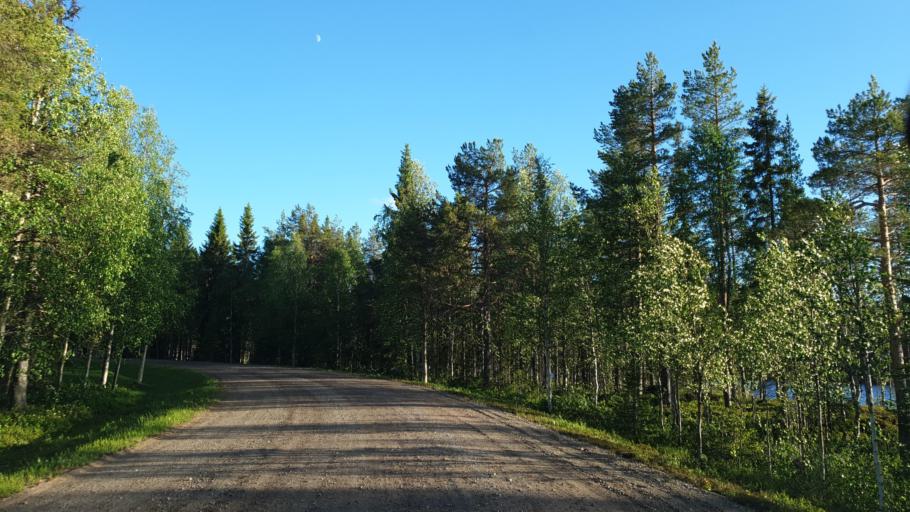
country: SE
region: Norrbotten
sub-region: Arvidsjaurs Kommun
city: Arvidsjaur
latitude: 65.7096
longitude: 18.7058
